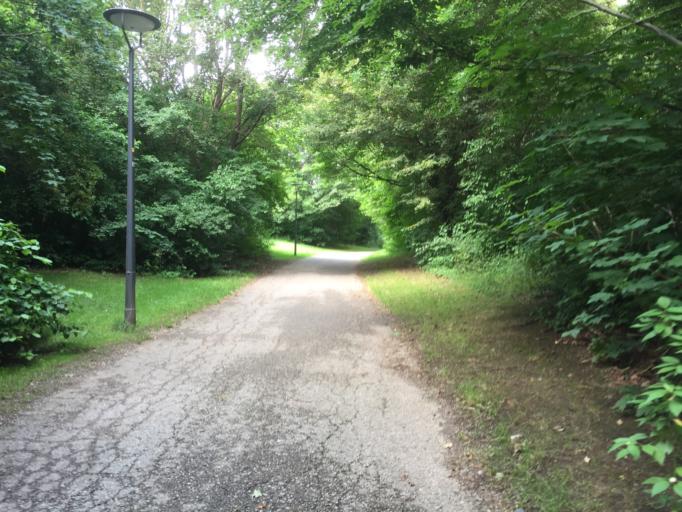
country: DE
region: Bavaria
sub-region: Upper Bavaria
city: Bogenhausen
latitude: 48.1126
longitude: 11.6313
